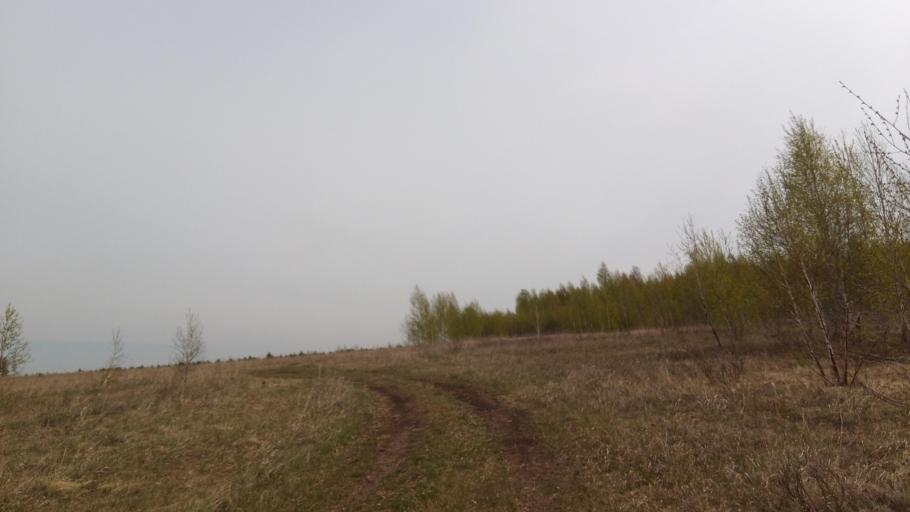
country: RU
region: Chelyabinsk
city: Timiryazevskiy
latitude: 55.0152
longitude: 60.8622
